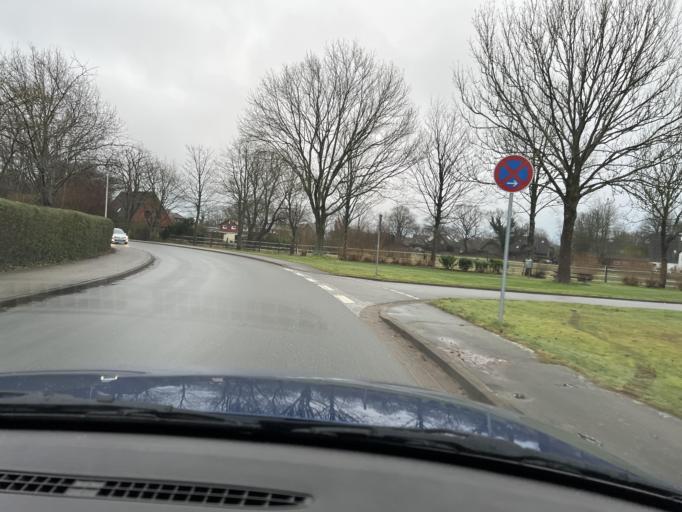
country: DE
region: Schleswig-Holstein
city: Wesseln
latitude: 54.2063
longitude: 9.0771
